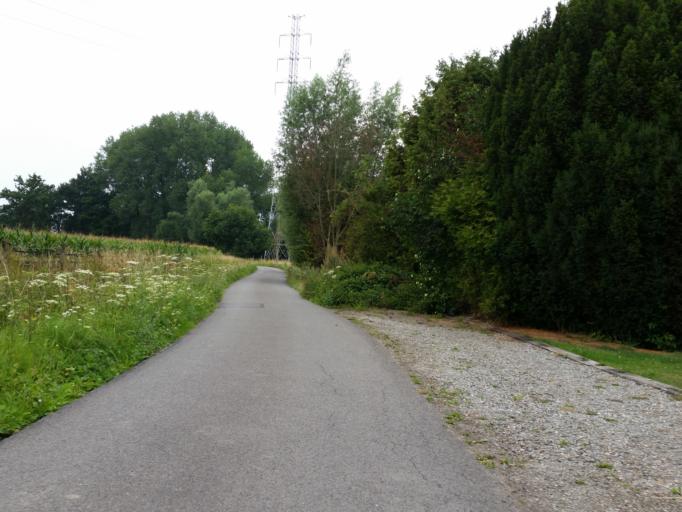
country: BE
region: Flanders
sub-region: Provincie Vlaams-Brabant
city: Vilvoorde
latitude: 50.9546
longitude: 4.4444
